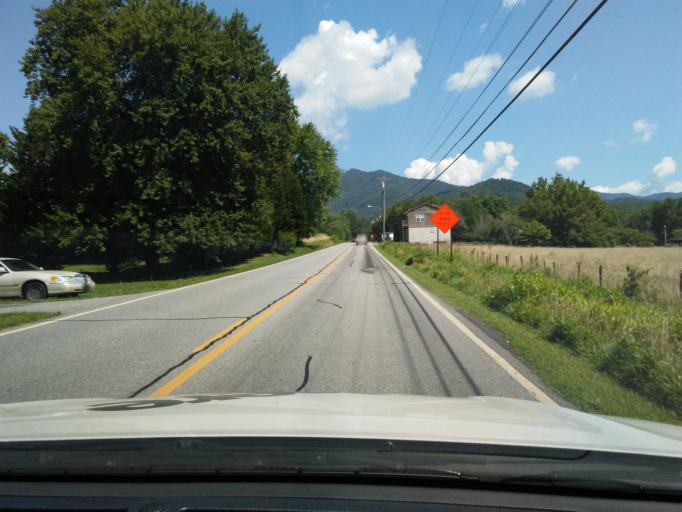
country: US
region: Georgia
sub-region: Towns County
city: Hiawassee
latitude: 34.9374
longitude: -83.8533
